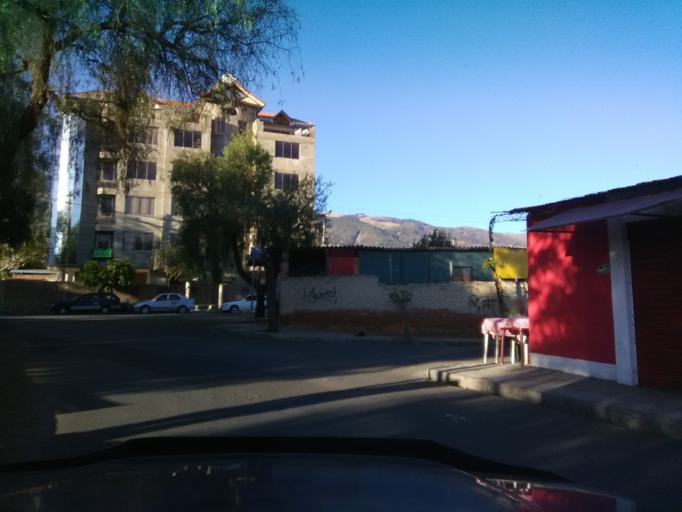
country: BO
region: Cochabamba
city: Cochabamba
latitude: -17.3624
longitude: -66.1854
